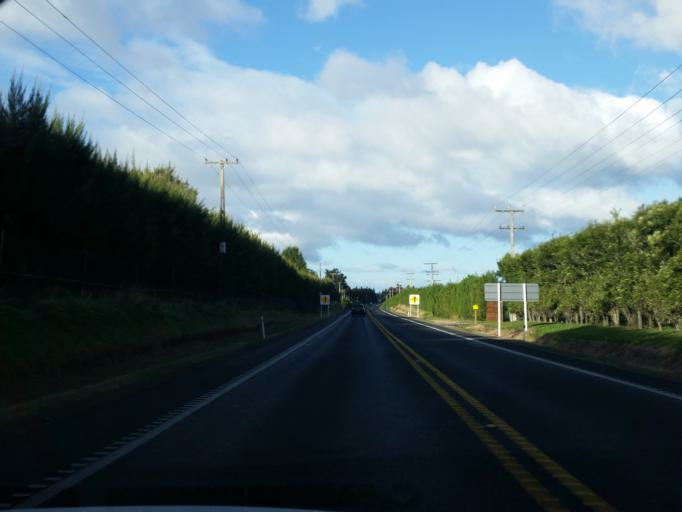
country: NZ
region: Bay of Plenty
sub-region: Western Bay of Plenty District
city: Katikati
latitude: -37.6031
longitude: 175.9286
